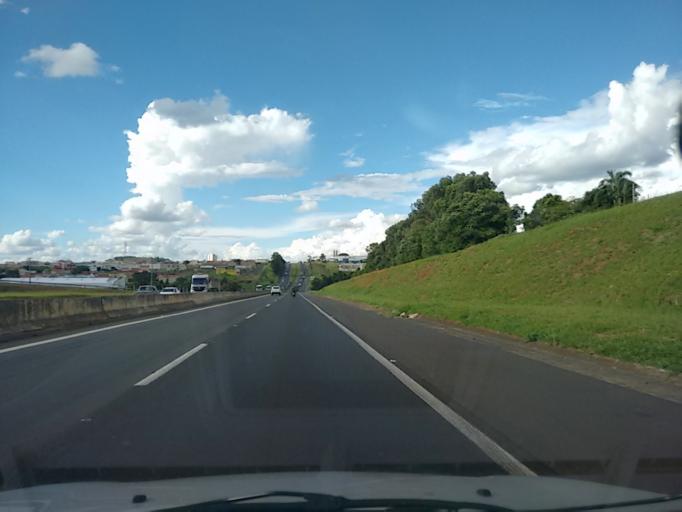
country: BR
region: Sao Paulo
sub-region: Sao Carlos
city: Sao Carlos
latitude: -22.0363
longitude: -47.8609
